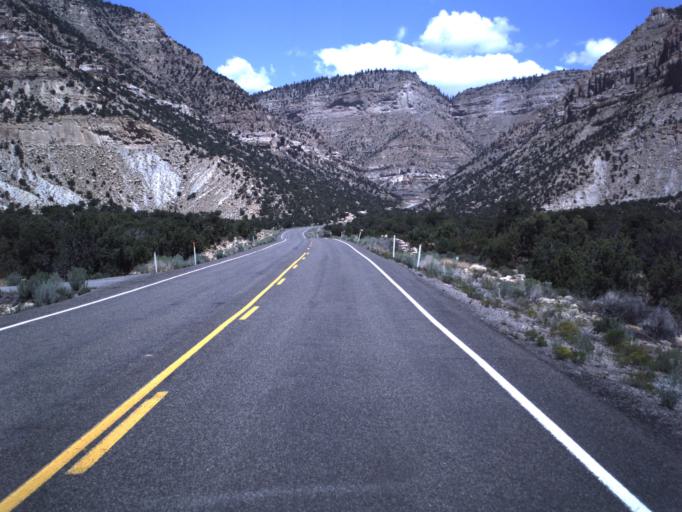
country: US
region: Utah
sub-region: Emery County
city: Orangeville
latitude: 39.3011
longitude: -111.1177
